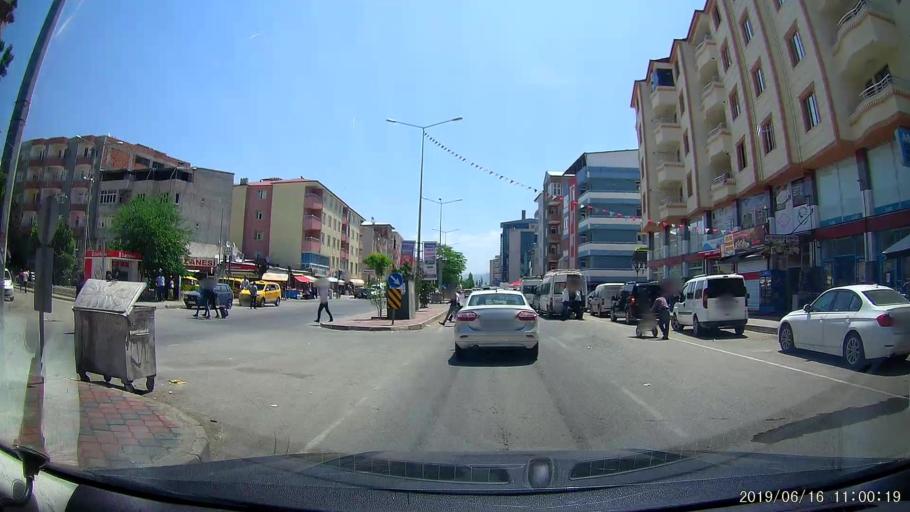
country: TR
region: Igdir
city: Igdir
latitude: 39.9187
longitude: 44.0430
